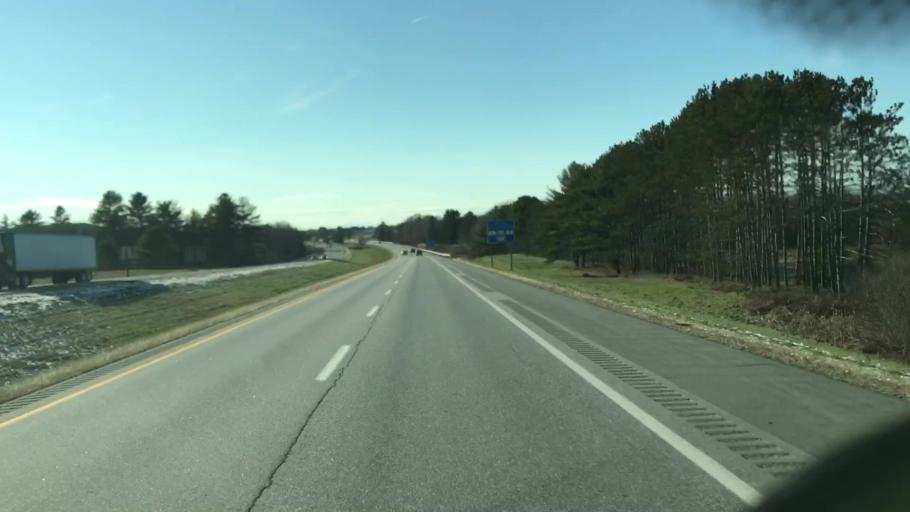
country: US
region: Maine
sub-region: Penobscot County
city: Hampden
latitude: 44.7769
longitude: -68.8458
